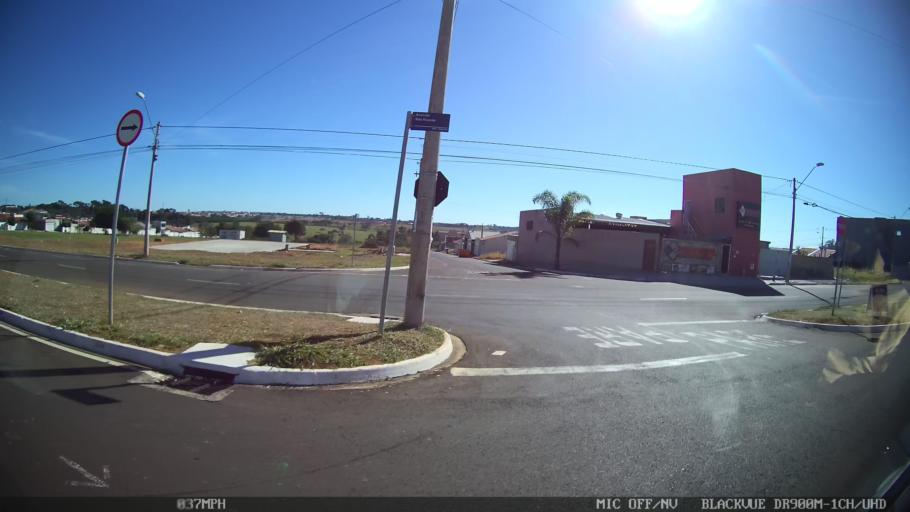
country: BR
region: Sao Paulo
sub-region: Franca
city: Franca
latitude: -20.5644
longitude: -47.3485
